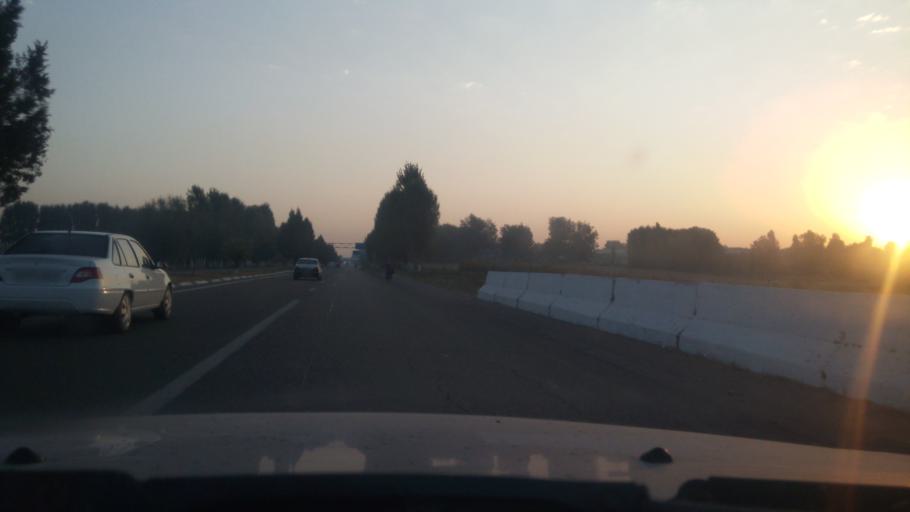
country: UZ
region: Toshkent
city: Amir Timur
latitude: 41.0798
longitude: 68.9372
